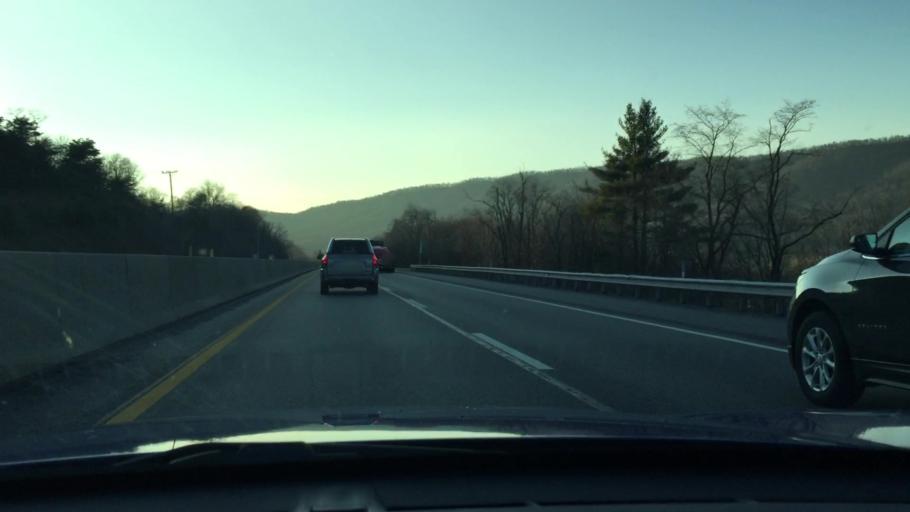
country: US
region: Pennsylvania
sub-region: Franklin County
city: Doylestown
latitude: 40.1583
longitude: -77.6910
